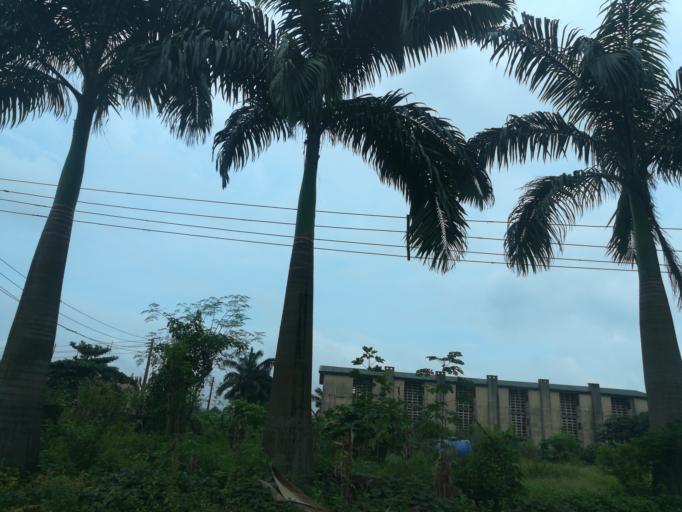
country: NG
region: Lagos
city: Oshodi
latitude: 6.5688
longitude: 3.3541
